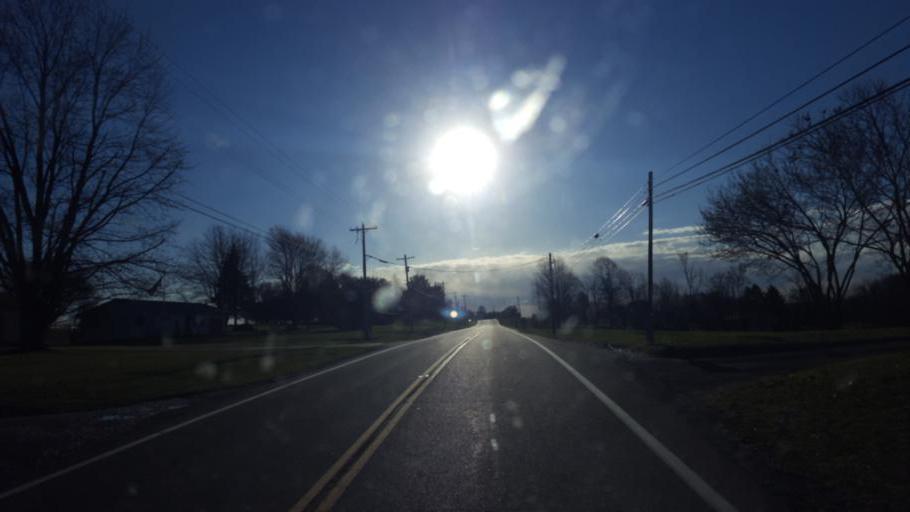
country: US
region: Ohio
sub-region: Wayne County
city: Shreve
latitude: 40.5949
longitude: -82.0985
